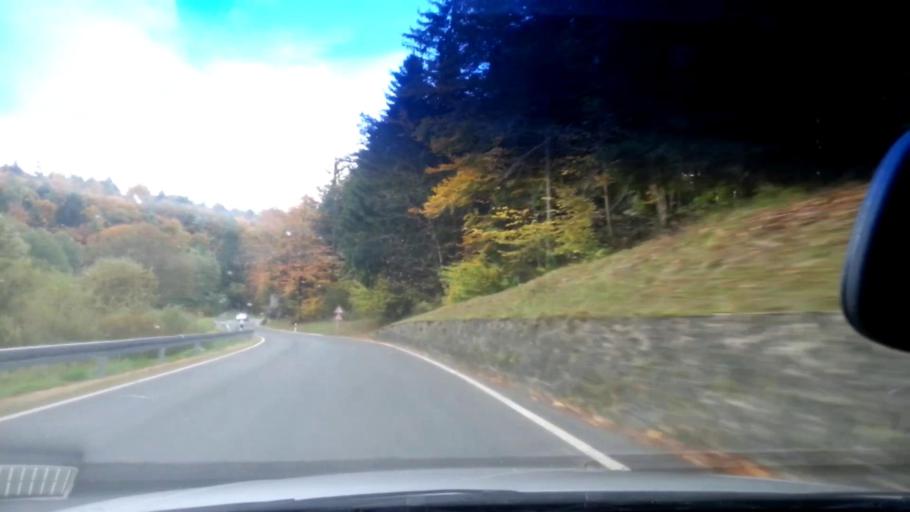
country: DE
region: Bavaria
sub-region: Upper Franconia
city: Wonsees
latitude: 49.9842
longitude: 11.2965
